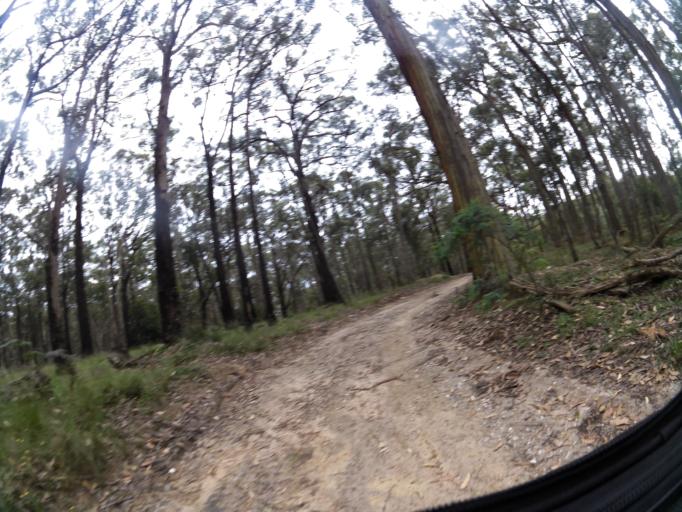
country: AU
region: Victoria
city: Brown Hill
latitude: -37.5156
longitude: 143.9141
